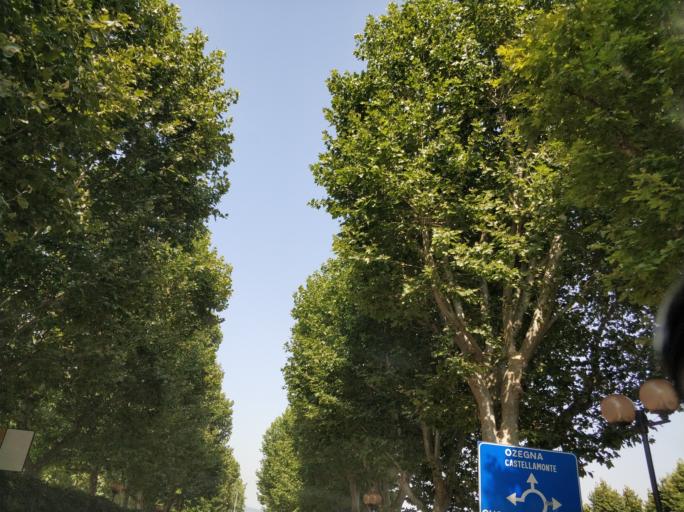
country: IT
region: Piedmont
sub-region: Provincia di Torino
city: Rivarolo Canavese
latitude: 45.3339
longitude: 7.7277
